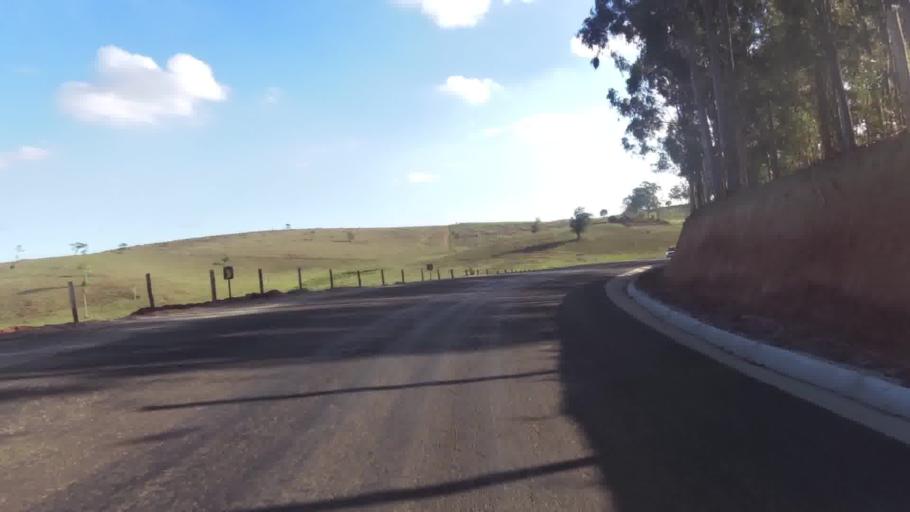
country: BR
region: Espirito Santo
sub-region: Marataizes
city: Marataizes
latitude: -21.1290
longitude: -41.0497
